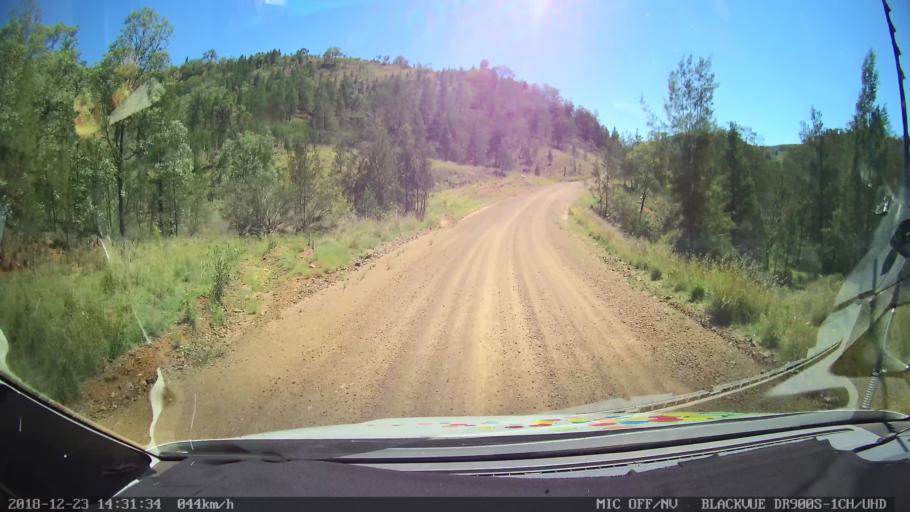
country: AU
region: New South Wales
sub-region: Tamworth Municipality
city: Manilla
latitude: -30.6030
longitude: 150.9253
